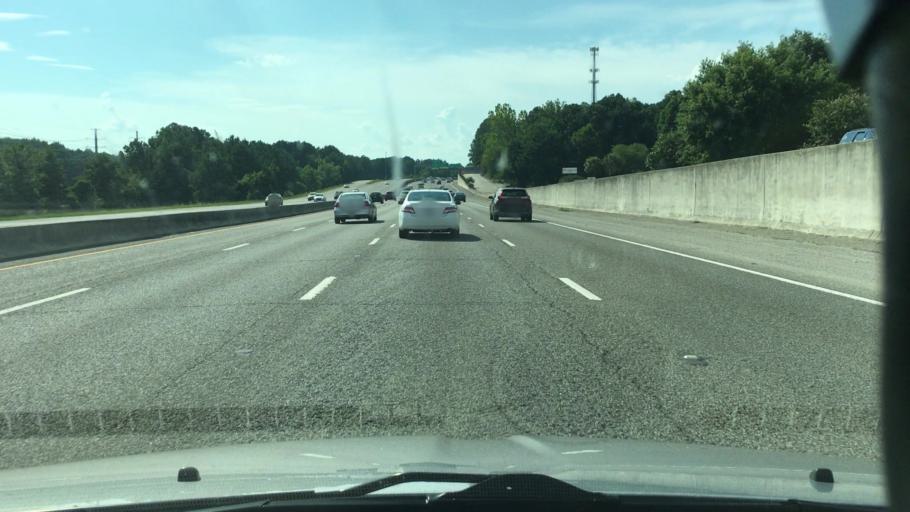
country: US
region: South Carolina
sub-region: Lexington County
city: West Columbia
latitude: 34.0163
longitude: -81.0865
